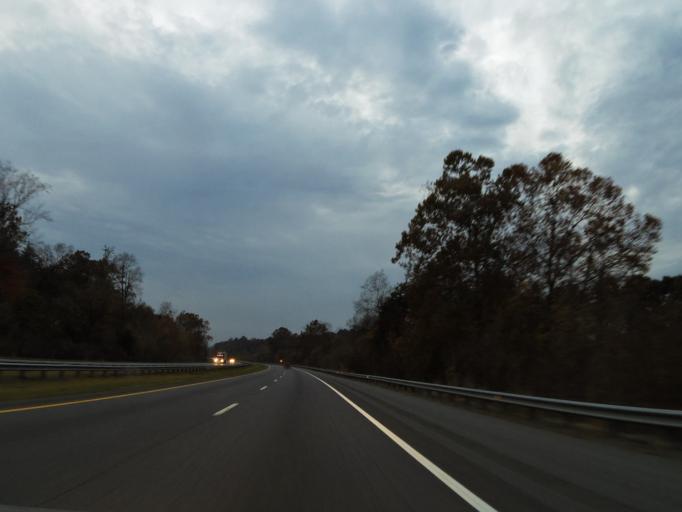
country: US
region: North Carolina
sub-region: Burke County
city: Glen Alpine
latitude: 35.6959
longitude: -81.8688
